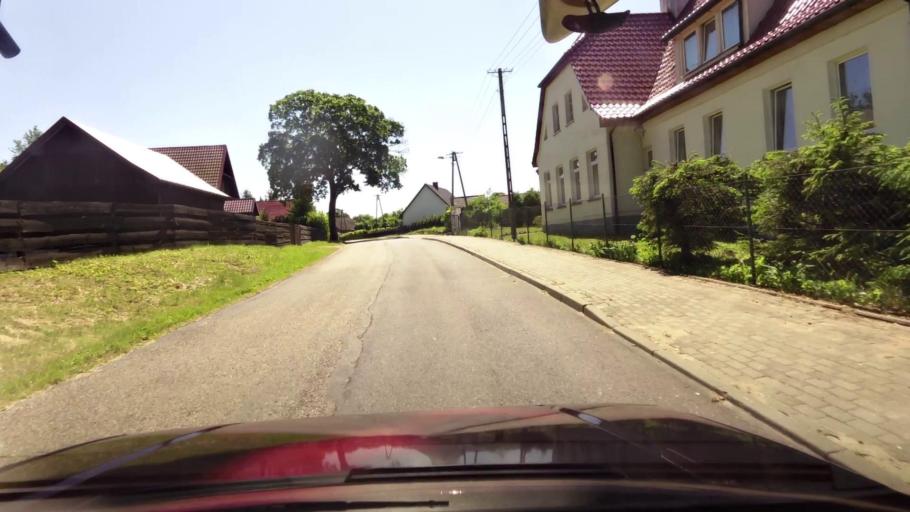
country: PL
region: West Pomeranian Voivodeship
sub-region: Powiat koszalinski
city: Bobolice
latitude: 53.9964
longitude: 16.6849
